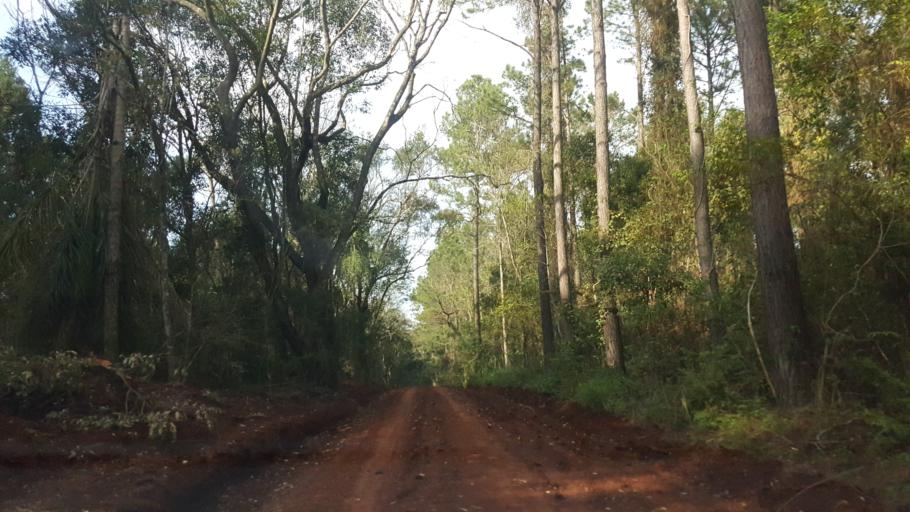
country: AR
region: Misiones
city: Capiovi
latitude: -26.8993
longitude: -55.1071
